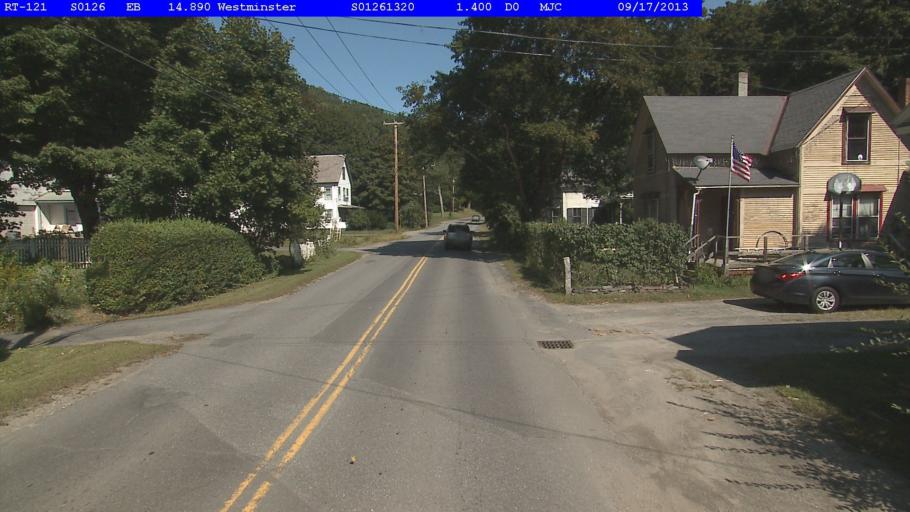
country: US
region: Vermont
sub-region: Windham County
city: Bellows Falls
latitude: 43.1200
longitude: -72.4536
